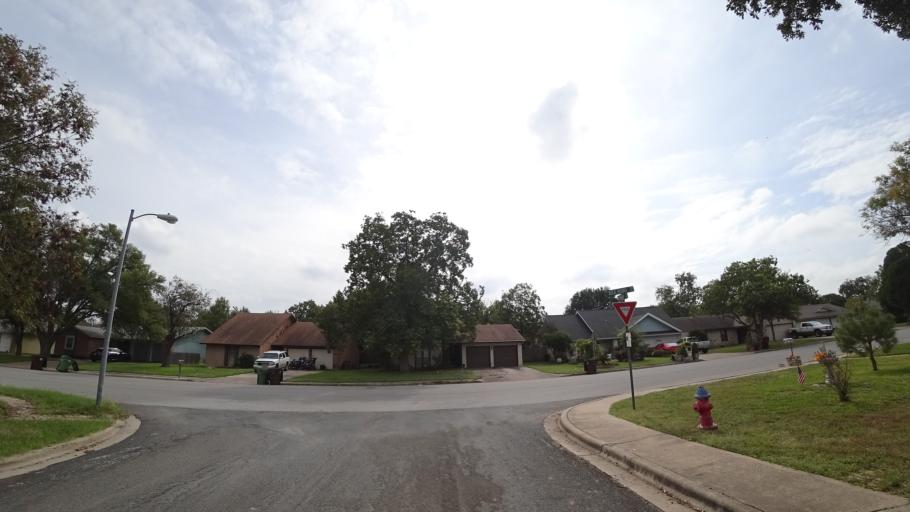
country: US
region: Texas
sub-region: Williamson County
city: Round Rock
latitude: 30.4940
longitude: -97.6826
